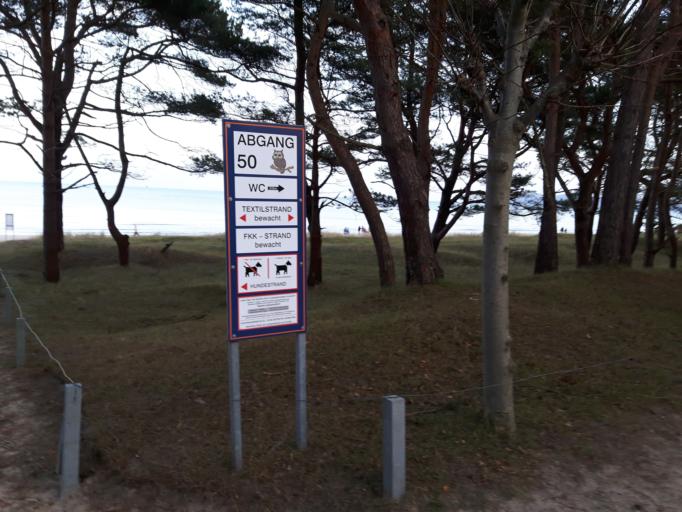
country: DE
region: Mecklenburg-Vorpommern
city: Ostseebad Binz
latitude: 54.4151
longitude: 13.5960
